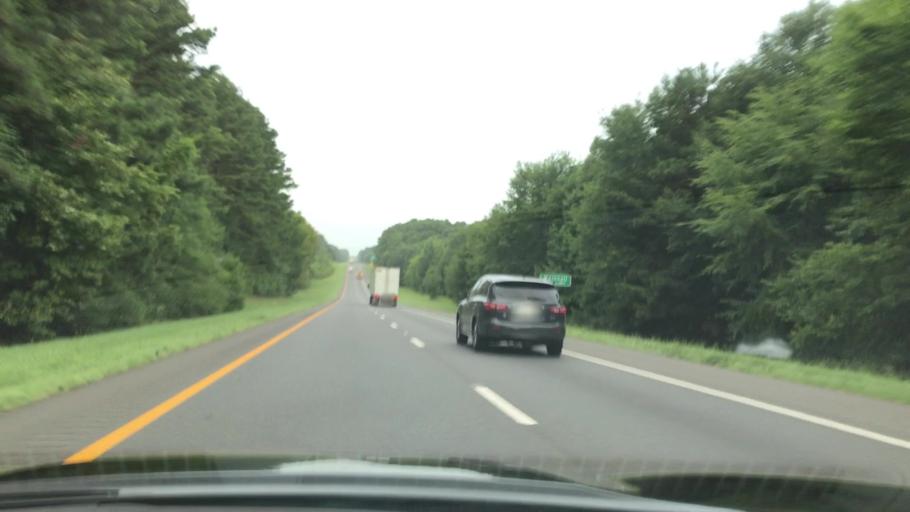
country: US
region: Texas
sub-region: Harrison County
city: Marshall
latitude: 32.4903
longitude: -94.3807
